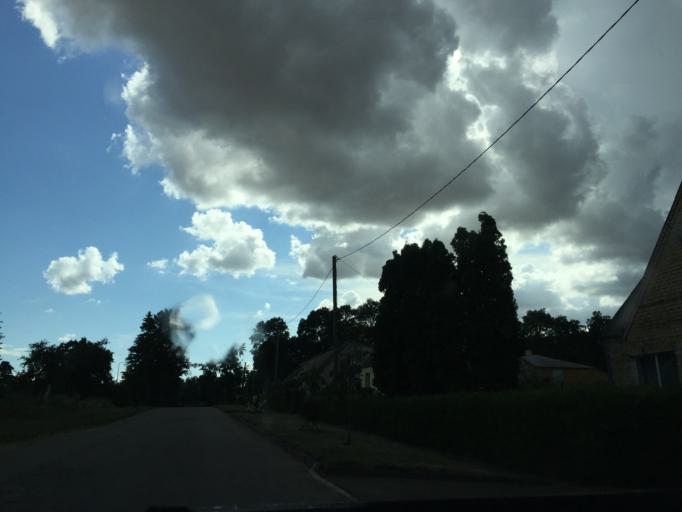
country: LV
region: Tervete
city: Zelmeni
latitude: 56.3075
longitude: 23.3909
